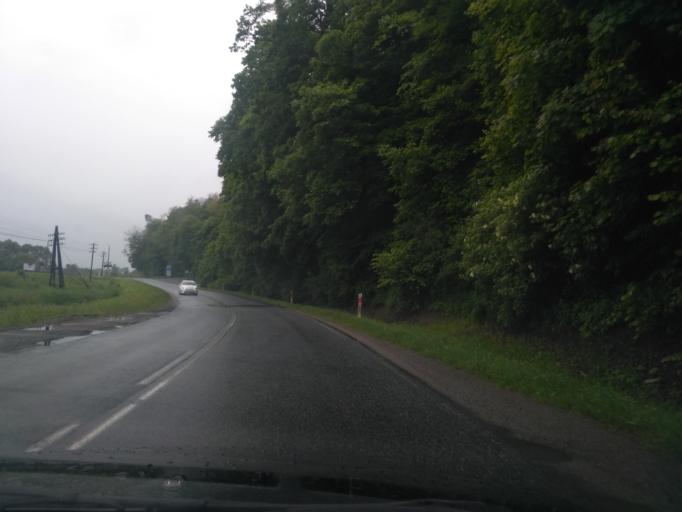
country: PL
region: Subcarpathian Voivodeship
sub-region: Powiat krosnienski
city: Leki
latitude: 49.8116
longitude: 21.6353
